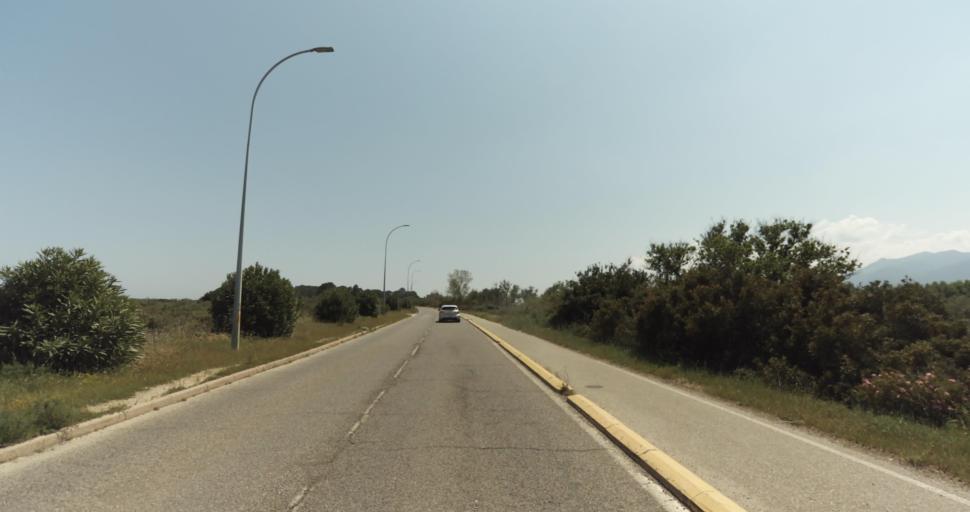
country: FR
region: Corsica
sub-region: Departement de la Haute-Corse
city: Biguglia
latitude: 42.6526
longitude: 9.4506
